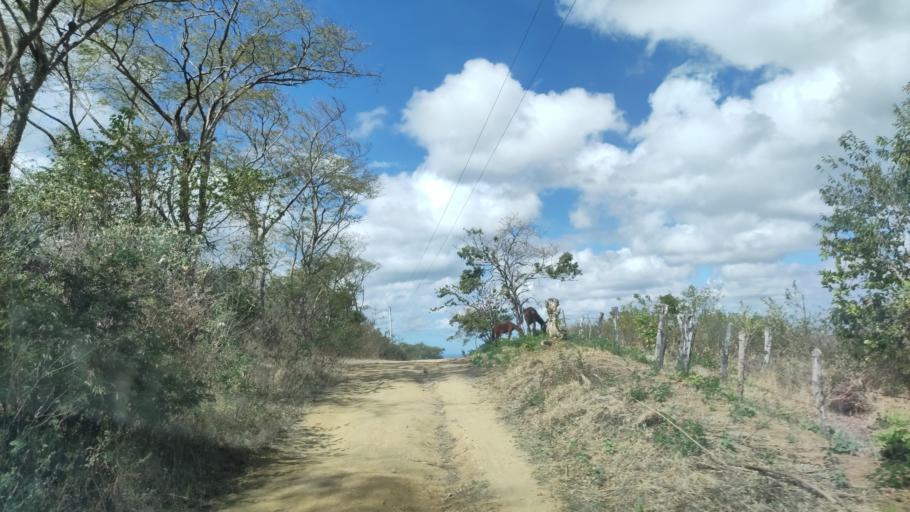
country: NI
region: Carazo
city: Santa Teresa
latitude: 11.6521
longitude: -86.2060
